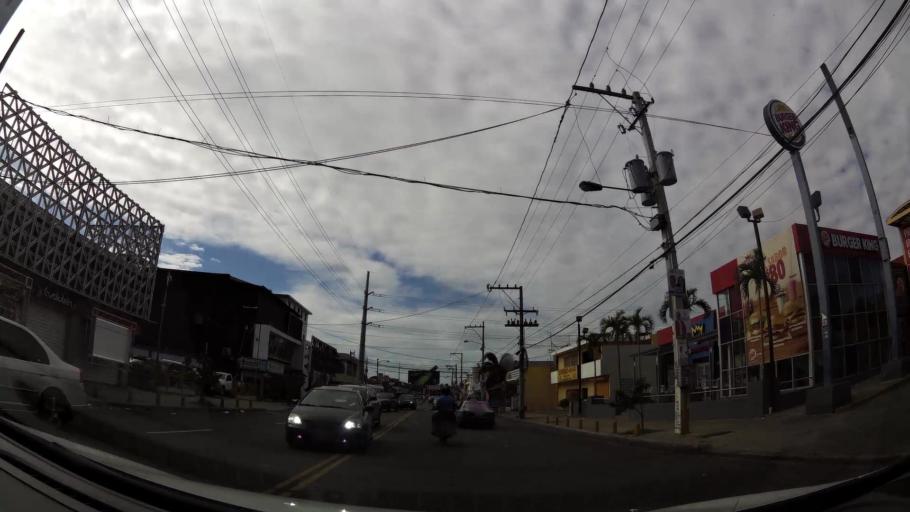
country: DO
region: Santo Domingo
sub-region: Santo Domingo
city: Santo Domingo Este
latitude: 18.4870
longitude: -69.8701
